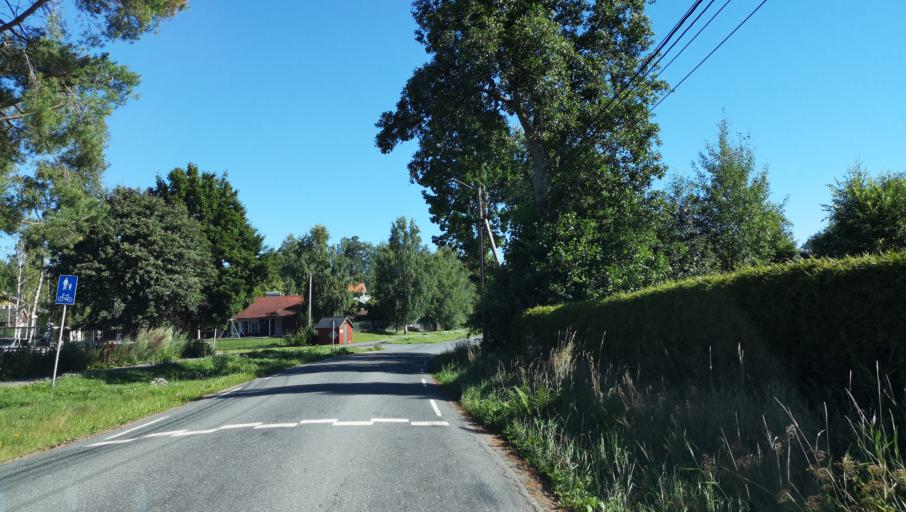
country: NO
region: Ostfold
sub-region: Hobol
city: Knappstad
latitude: 59.6256
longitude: 11.0252
